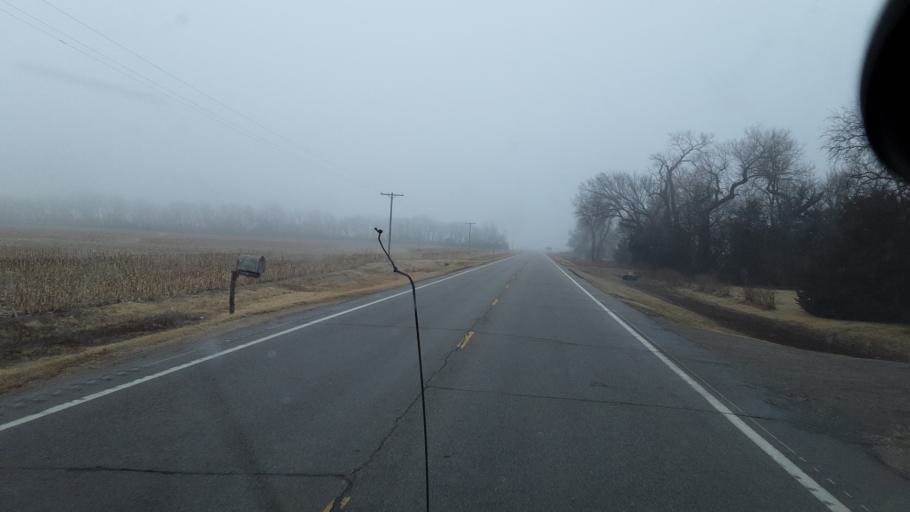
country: US
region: Kansas
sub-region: Reno County
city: South Hutchinson
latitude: 37.9456
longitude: -97.9404
